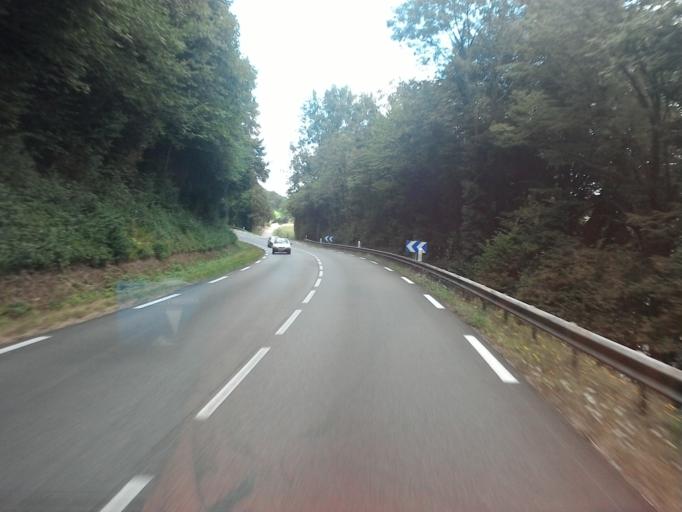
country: FR
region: Rhone-Alpes
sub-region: Departement de l'Ain
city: Saint-Sorlin-en-Bugey
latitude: 45.8683
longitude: 5.3782
